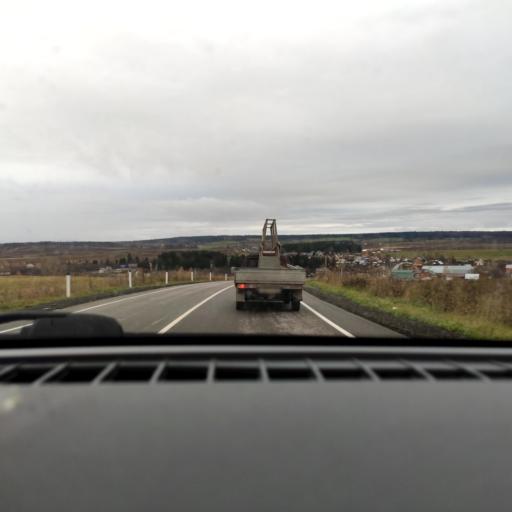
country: RU
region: Perm
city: Ferma
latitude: 57.9211
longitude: 56.3202
